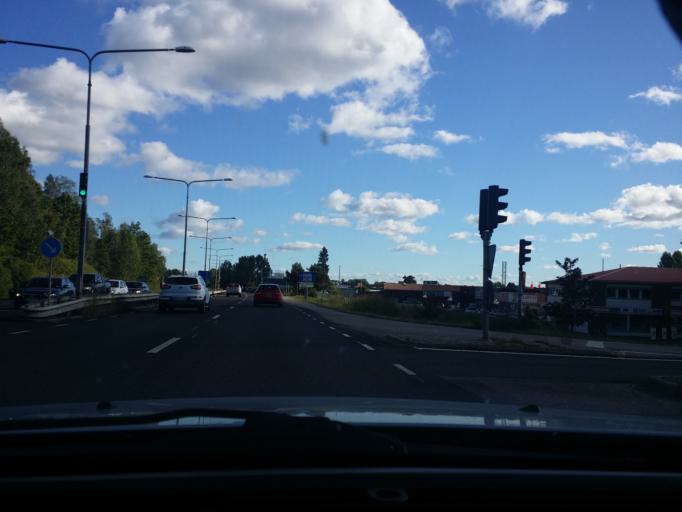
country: SE
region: Vaestmanland
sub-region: Vasteras
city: Vasteras
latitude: 59.6076
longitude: 16.4812
